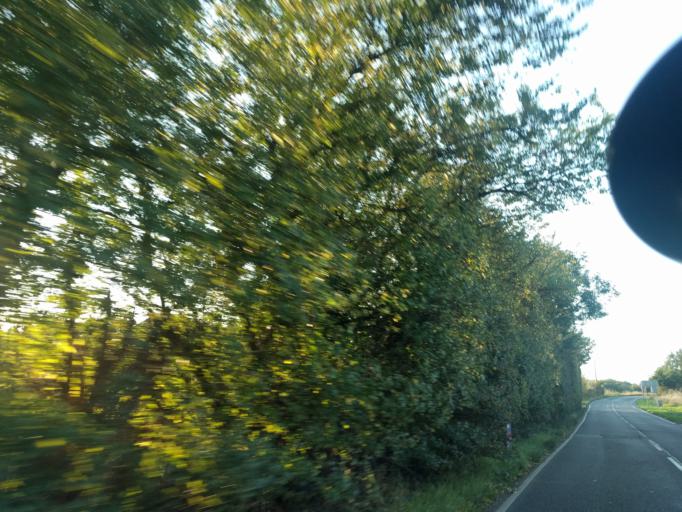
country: GB
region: England
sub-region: Essex
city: Witham
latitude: 51.8156
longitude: 0.6310
